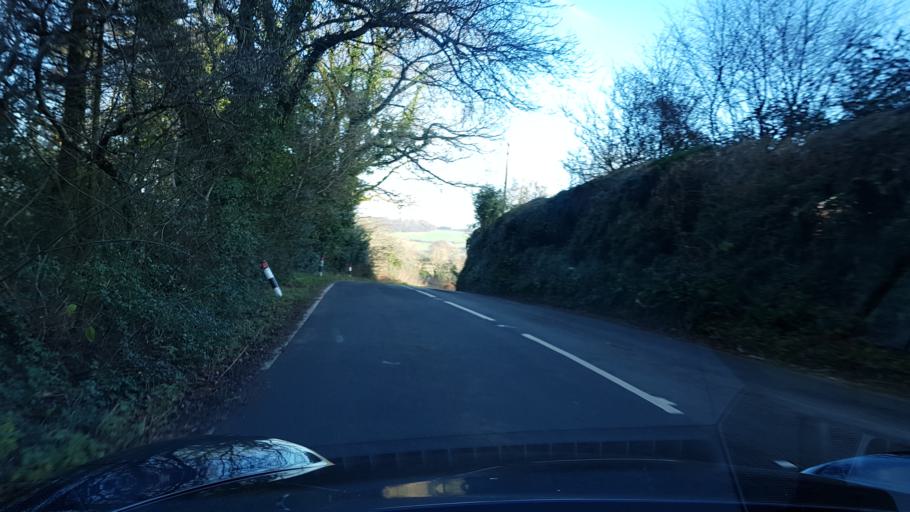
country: GB
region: England
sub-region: Dorset
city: Lyme Regis
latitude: 50.7905
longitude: -2.8907
